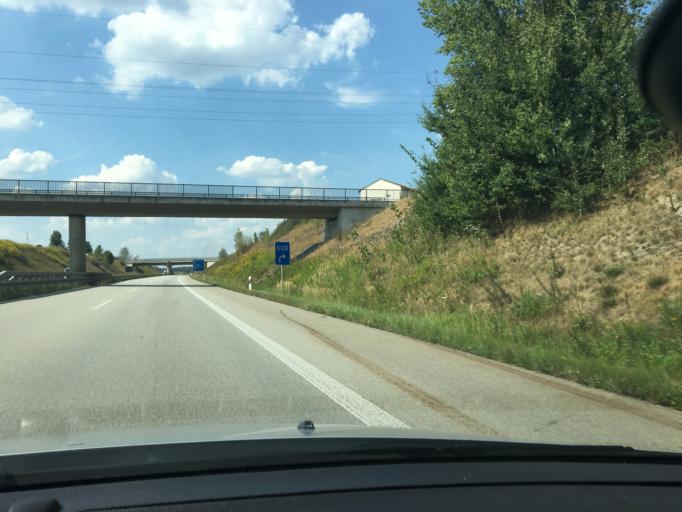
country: DE
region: Bavaria
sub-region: Upper Bavaria
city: Aresing
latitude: 48.2590
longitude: 12.6194
